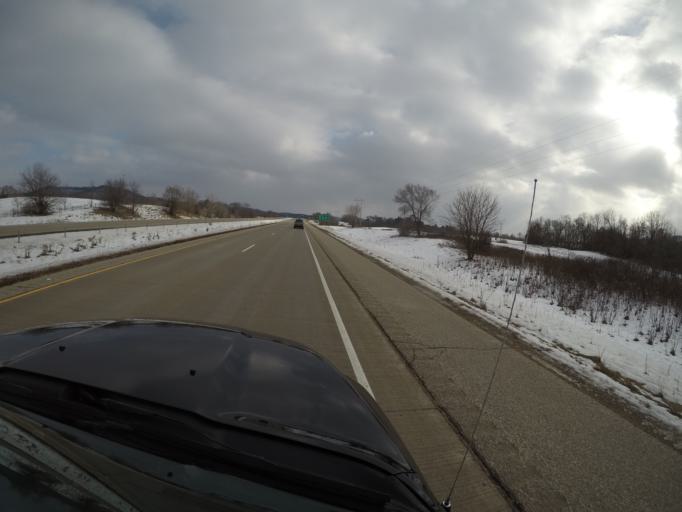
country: US
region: Wisconsin
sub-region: La Crosse County
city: Holmen
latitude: 43.9464
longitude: -91.2648
